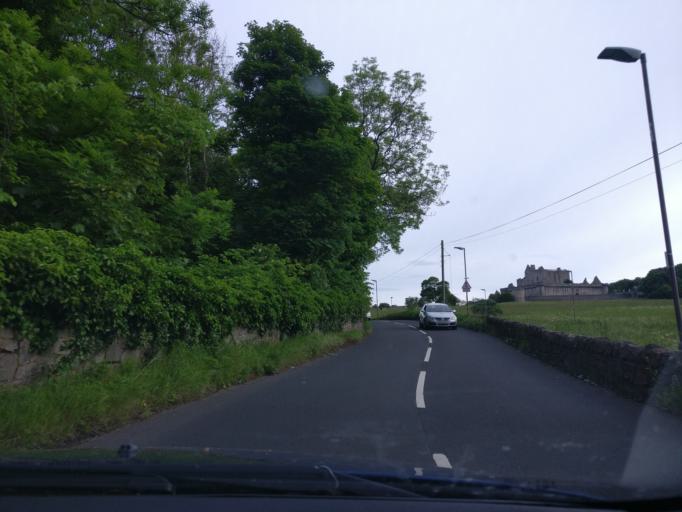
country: GB
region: Scotland
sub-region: West Lothian
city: Seafield
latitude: 55.9280
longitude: -3.1384
